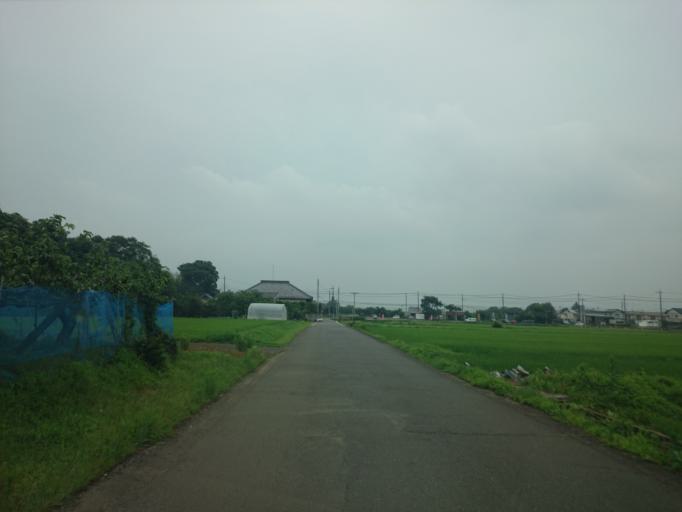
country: JP
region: Ibaraki
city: Tsukuba
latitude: 36.1056
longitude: 140.0684
